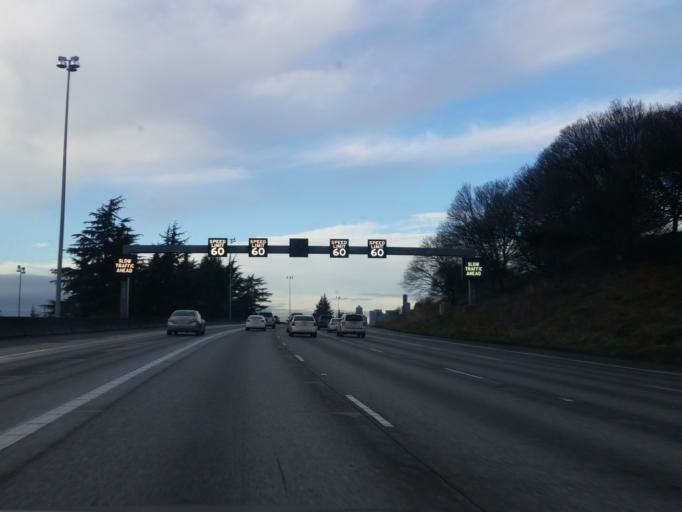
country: US
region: Washington
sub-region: King County
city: Seattle
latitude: 47.5578
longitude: -122.3206
